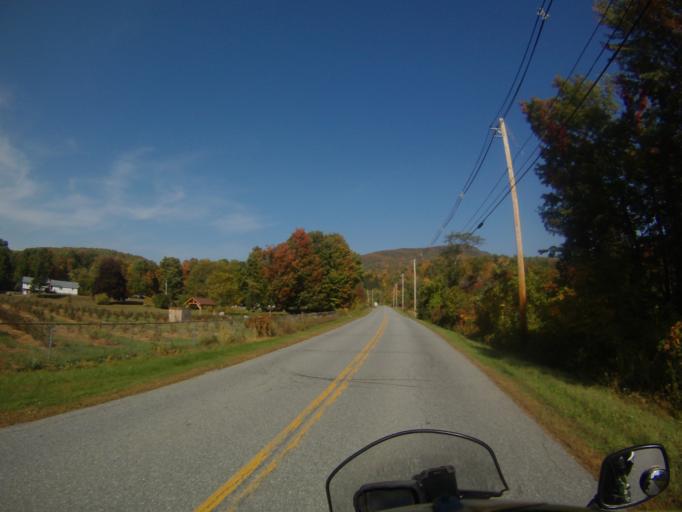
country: US
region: Vermont
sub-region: Addison County
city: Bristol
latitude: 44.1253
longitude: -73.0868
